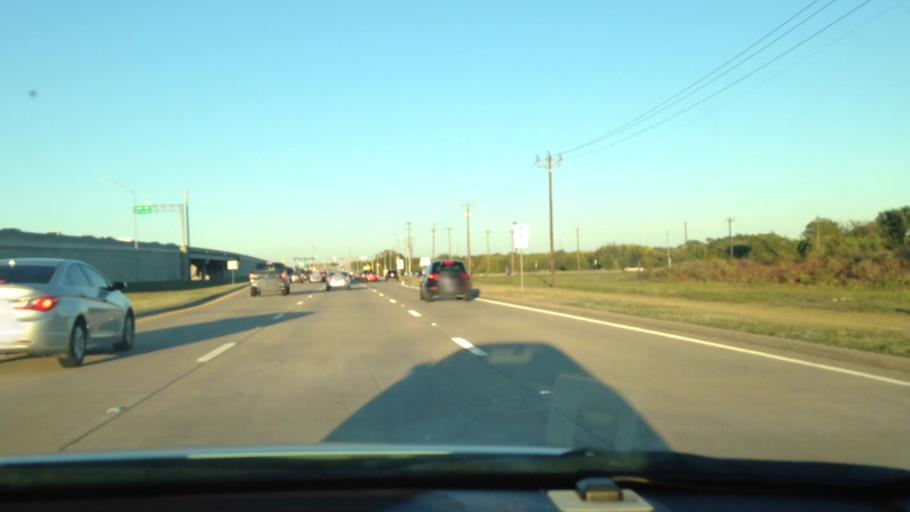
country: US
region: Texas
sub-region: Collin County
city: Frisco
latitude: 33.1025
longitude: -96.7909
